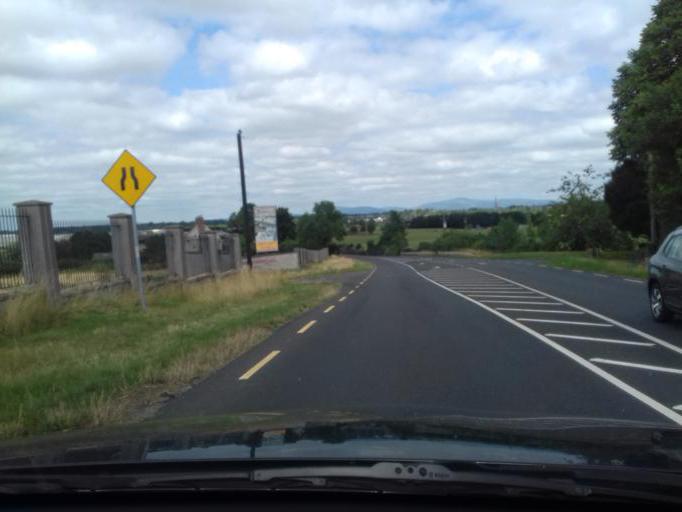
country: IE
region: Leinster
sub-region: County Carlow
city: Tullow
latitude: 52.7910
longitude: -6.7522
